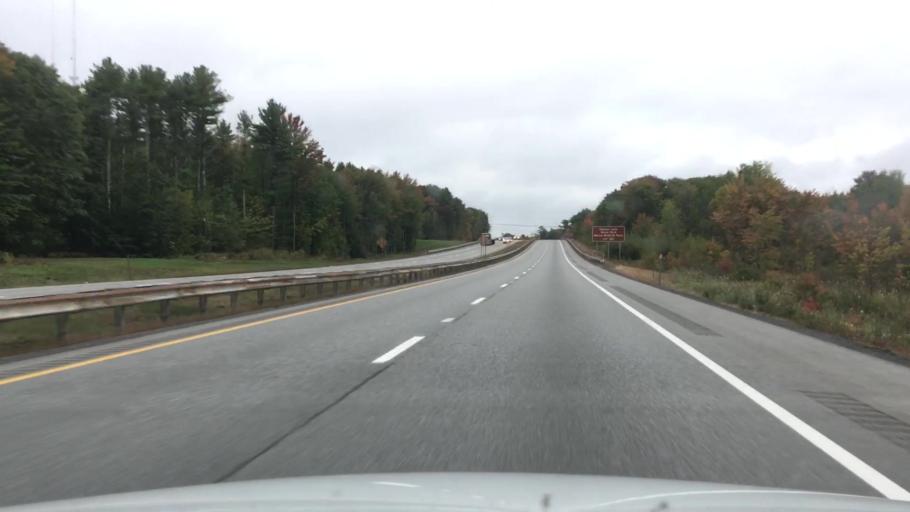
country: US
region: Maine
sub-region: Cumberland County
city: Cumberland Center
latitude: 43.8457
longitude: -70.3237
